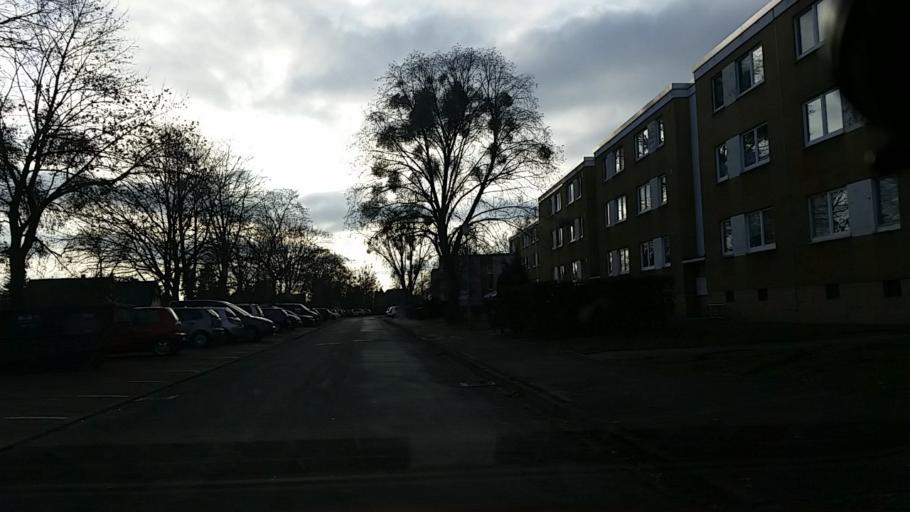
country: DE
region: Lower Saxony
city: Ruhen
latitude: 52.4519
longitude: 10.8532
